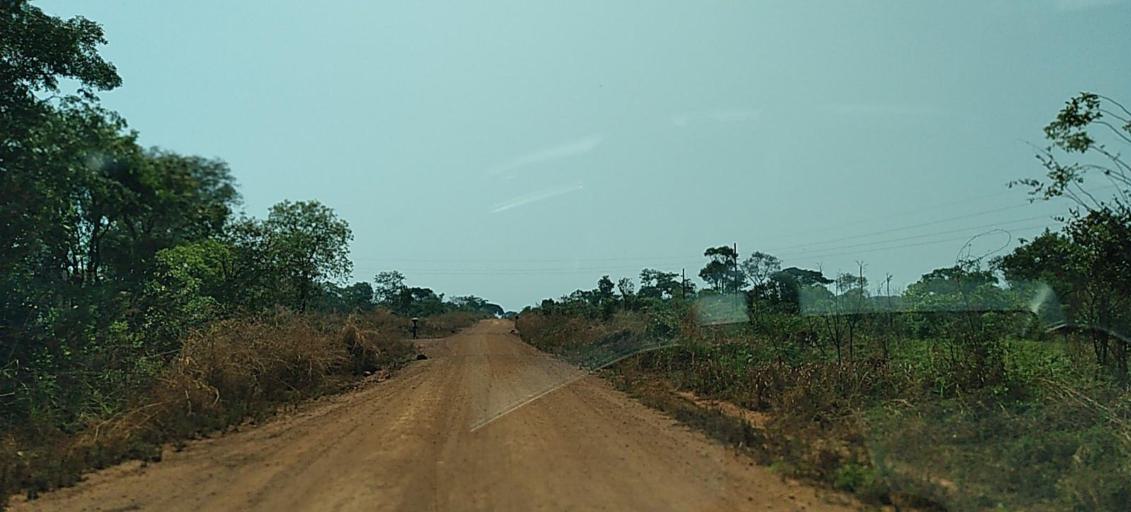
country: ZM
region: North-Western
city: Kansanshi
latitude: -12.0063
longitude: 26.5439
